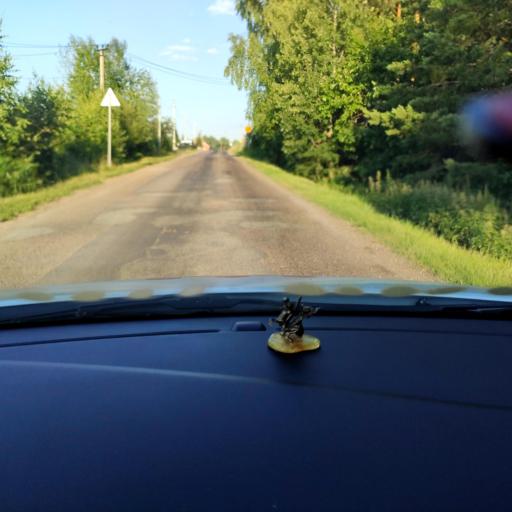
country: RU
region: Tatarstan
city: Pestretsy
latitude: 55.6162
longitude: 49.4882
